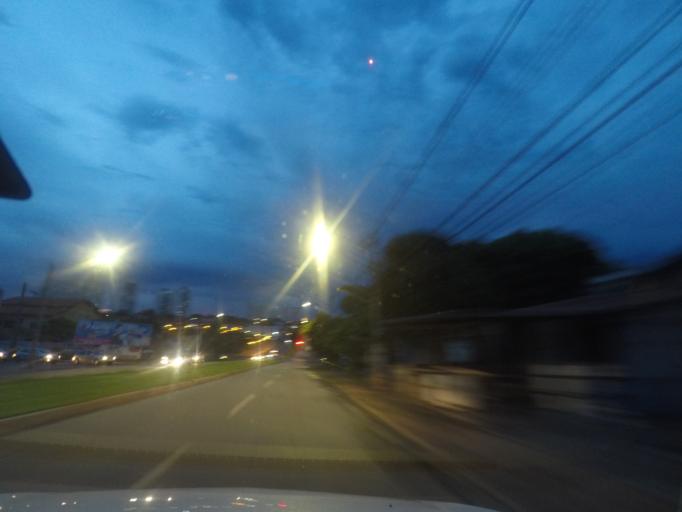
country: BR
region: Goias
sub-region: Goiania
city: Goiania
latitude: -16.7093
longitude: -49.3165
